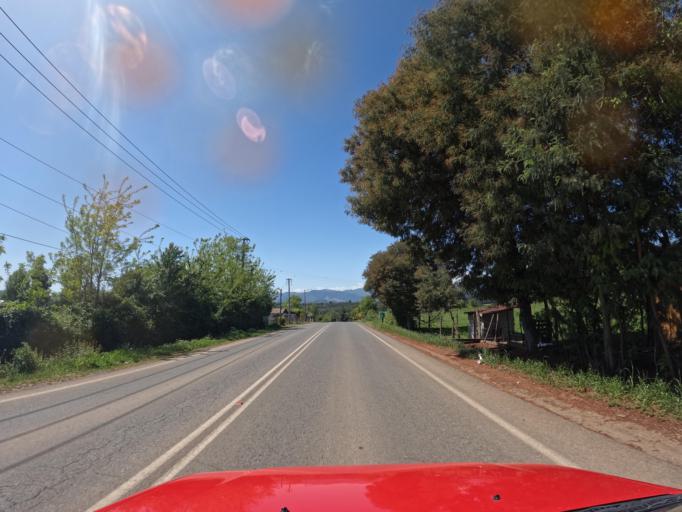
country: CL
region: Maule
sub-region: Provincia de Talca
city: San Clemente
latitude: -35.4906
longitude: -71.3047
